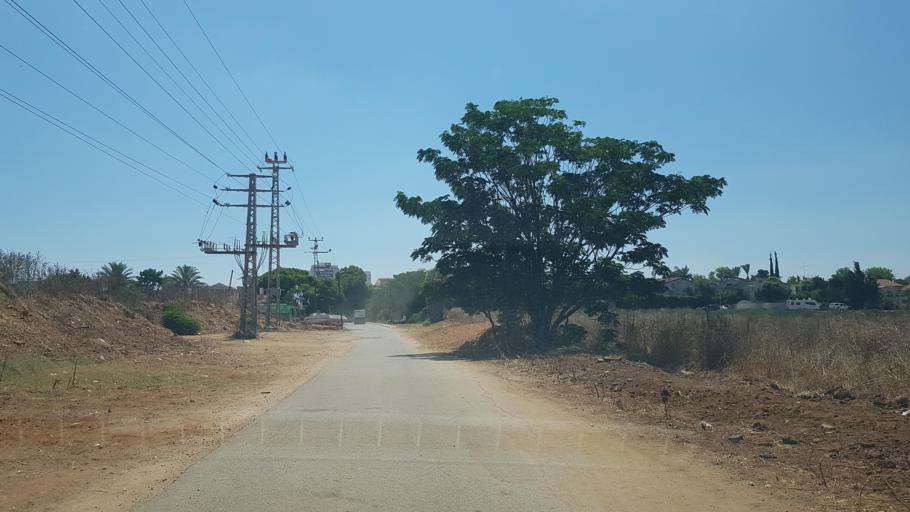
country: IL
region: Tel Aviv
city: Ramat HaSharon
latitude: 32.1541
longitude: 34.8327
